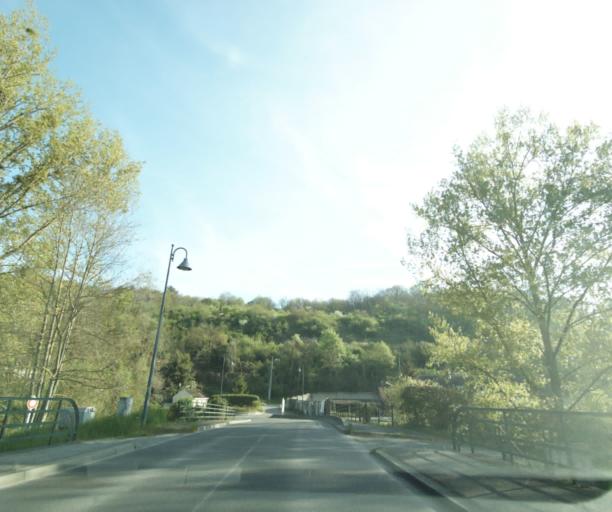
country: FR
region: Ile-de-France
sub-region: Departement de Seine-et-Marne
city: Moret-sur-Loing
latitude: 48.3768
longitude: 2.8201
